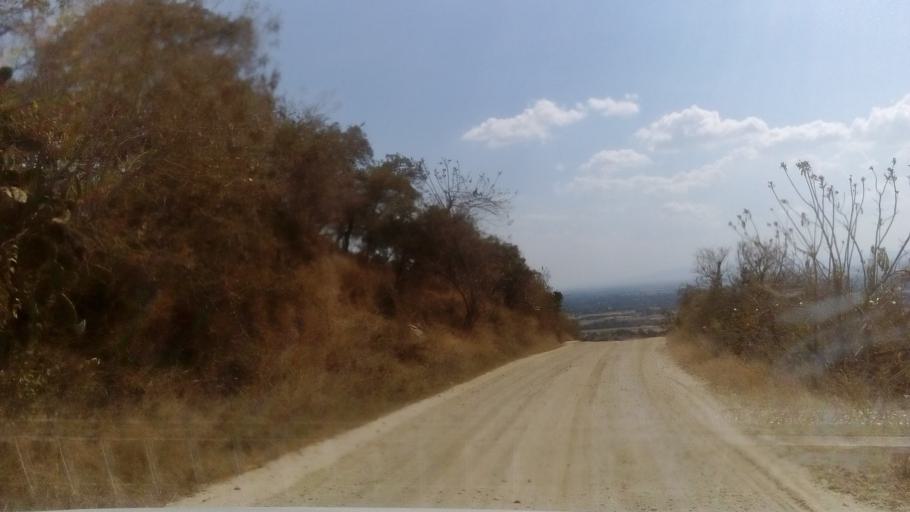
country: MX
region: Guanajuato
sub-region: Silao de la Victoria
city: Loma de Yerbabuena
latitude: 21.0704
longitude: -101.4561
